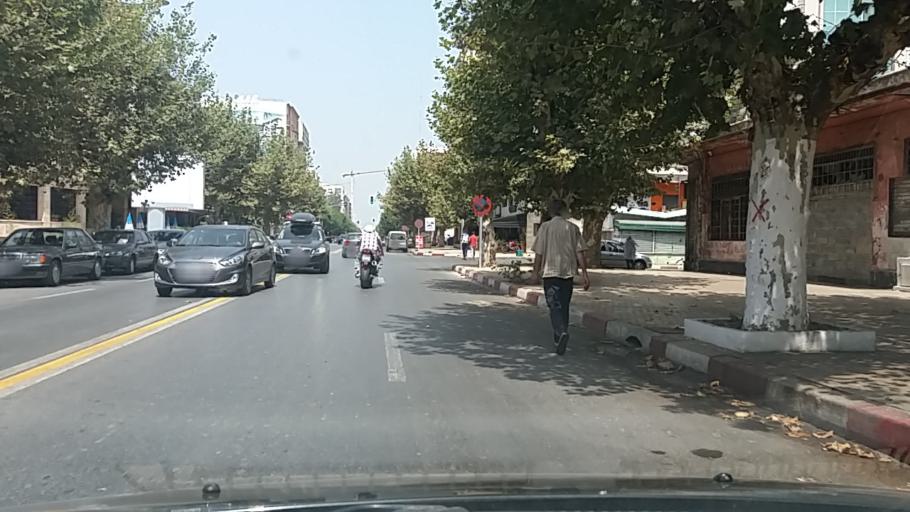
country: MA
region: Gharb-Chrarda-Beni Hssen
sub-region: Kenitra Province
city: Kenitra
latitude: 34.2605
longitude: -6.5850
